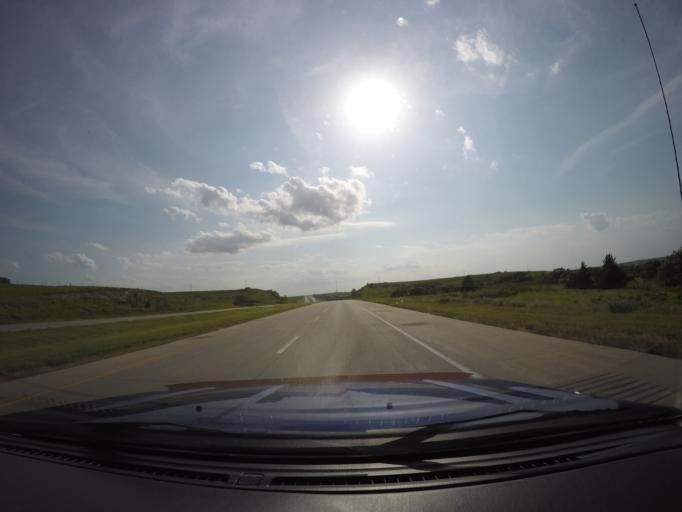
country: US
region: Kansas
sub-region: Riley County
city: Manhattan
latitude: 39.0690
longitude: -96.4893
